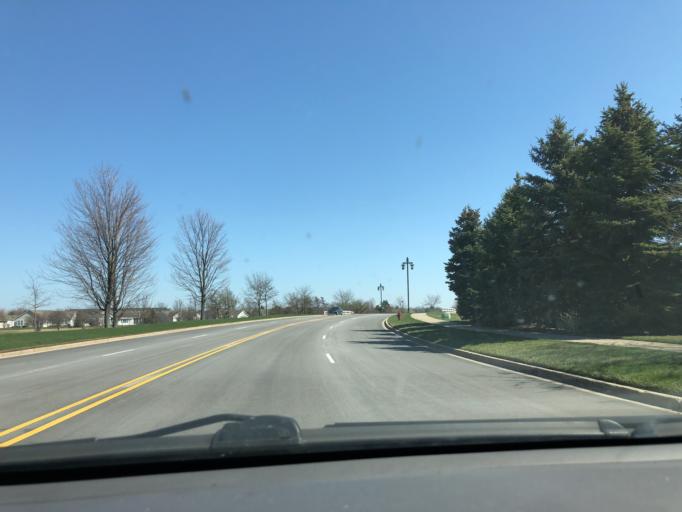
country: US
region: Illinois
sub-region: McHenry County
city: Huntley
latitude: 42.1546
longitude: -88.4468
